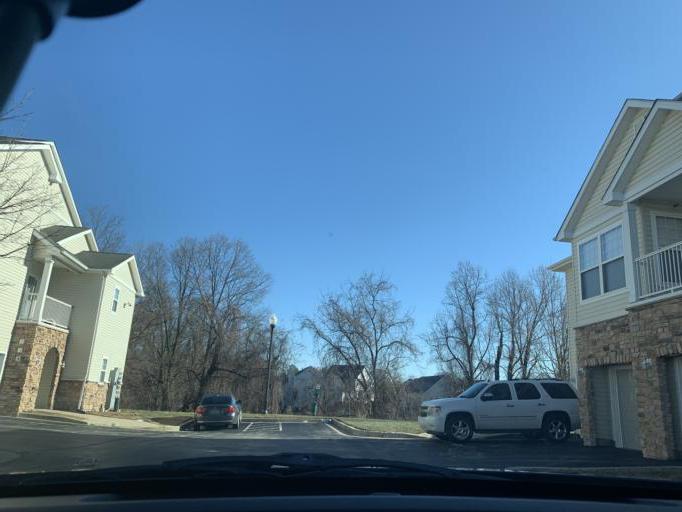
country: US
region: Maryland
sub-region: Baltimore County
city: Garrison
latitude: 39.3975
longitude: -76.7439
